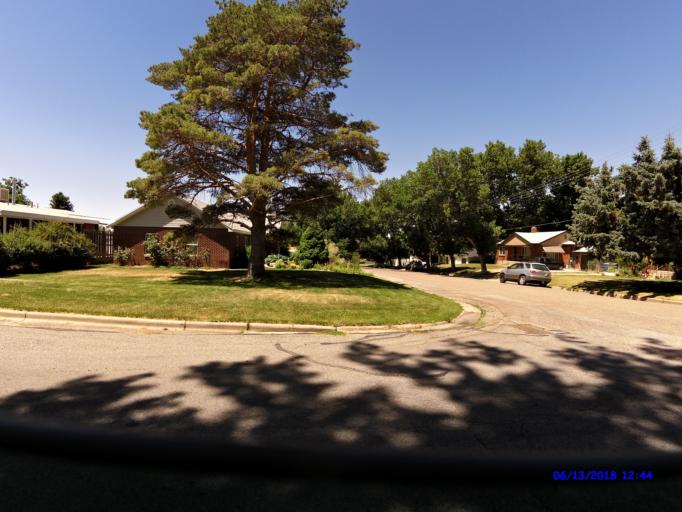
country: US
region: Utah
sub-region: Weber County
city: South Ogden
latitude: 41.1994
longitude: -111.9515
